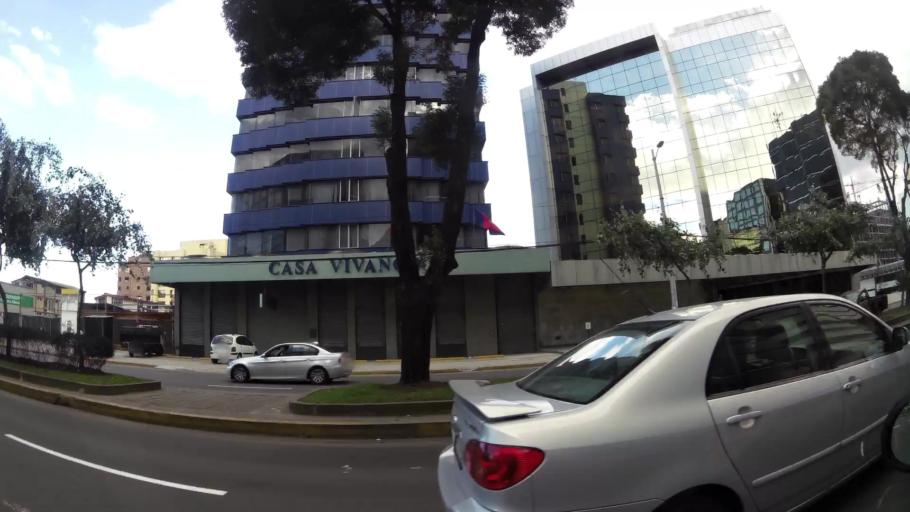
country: EC
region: Pichincha
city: Quito
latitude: -0.1709
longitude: -78.4848
